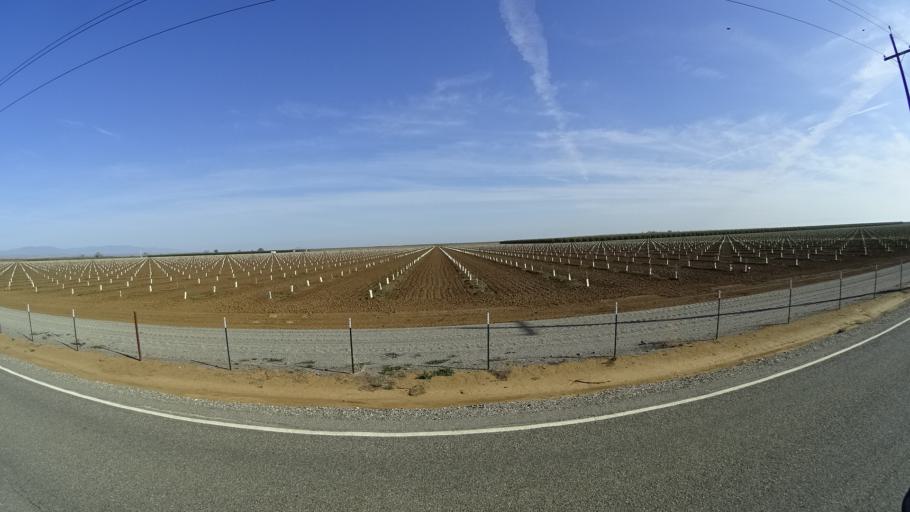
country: US
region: California
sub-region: Glenn County
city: Willows
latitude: 39.5388
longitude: -122.2420
